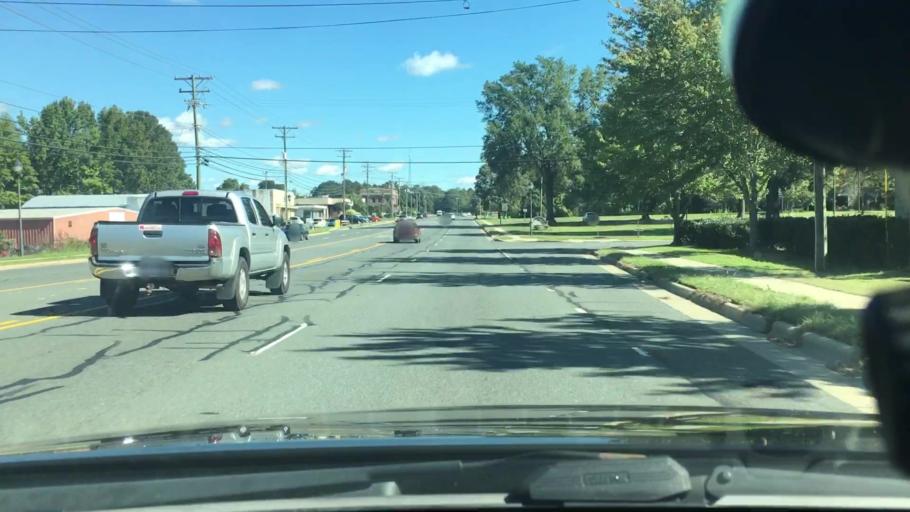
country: US
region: North Carolina
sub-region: Stanly County
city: Locust
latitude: 35.2562
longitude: -80.4337
